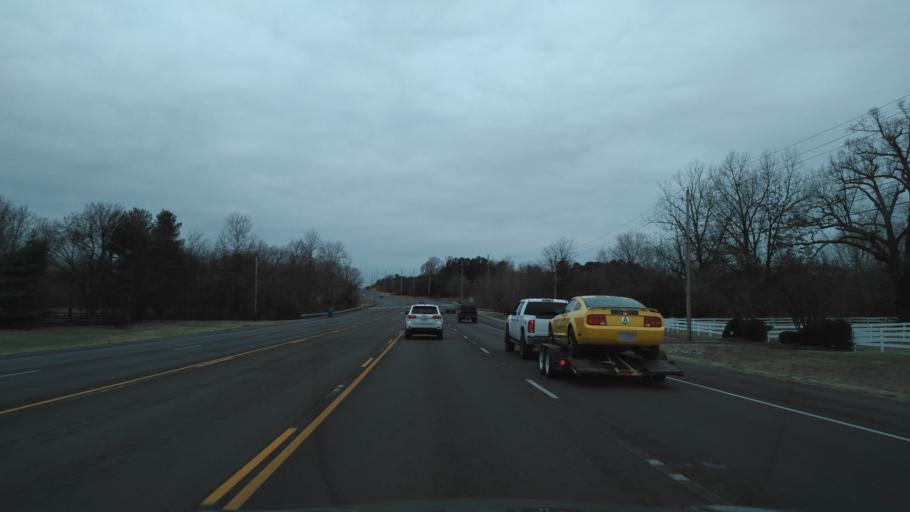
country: US
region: Kentucky
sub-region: McCracken County
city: Hendron
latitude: 37.0486
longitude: -88.6836
